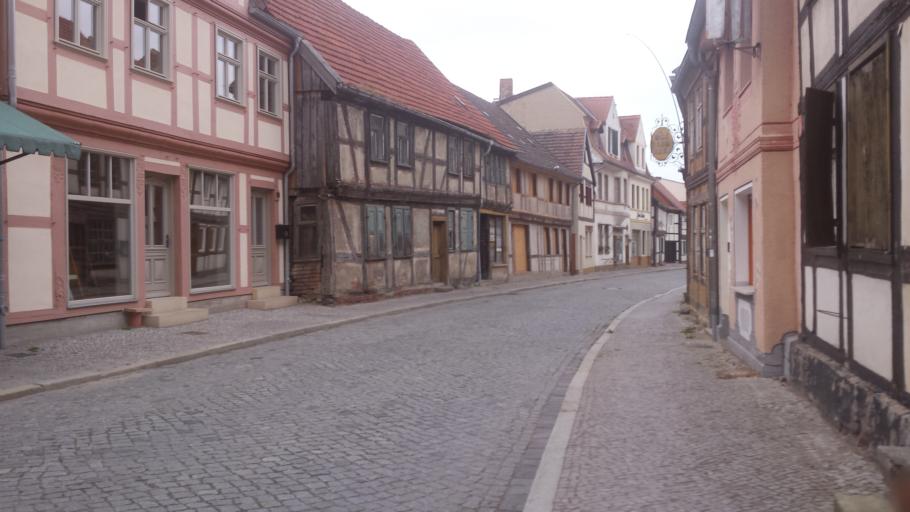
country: DE
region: Saxony-Anhalt
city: Tangermunde
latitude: 52.5439
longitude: 11.9757
